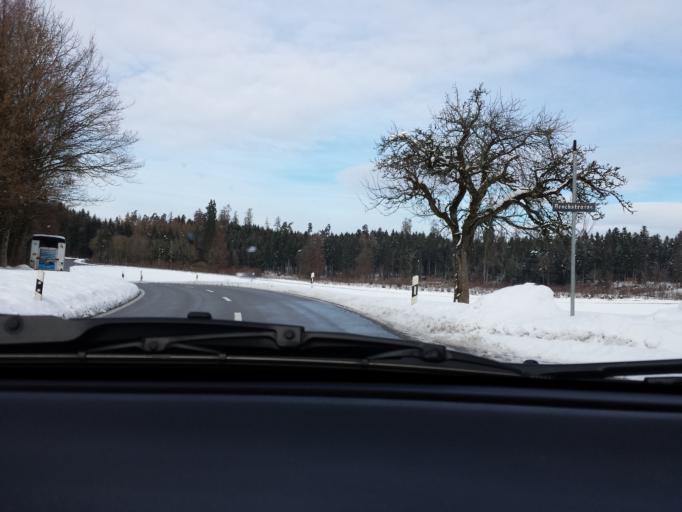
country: CH
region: Zurich
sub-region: Bezirk Hinwil
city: Bubikon
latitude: 47.2837
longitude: 8.8089
